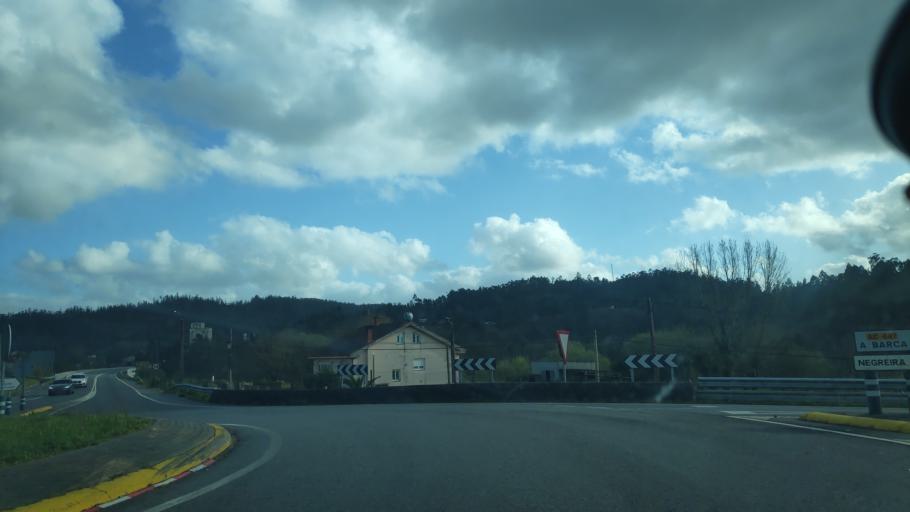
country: ES
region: Galicia
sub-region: Provincia da Coruna
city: Negreira
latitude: 42.9029
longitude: -8.7078
